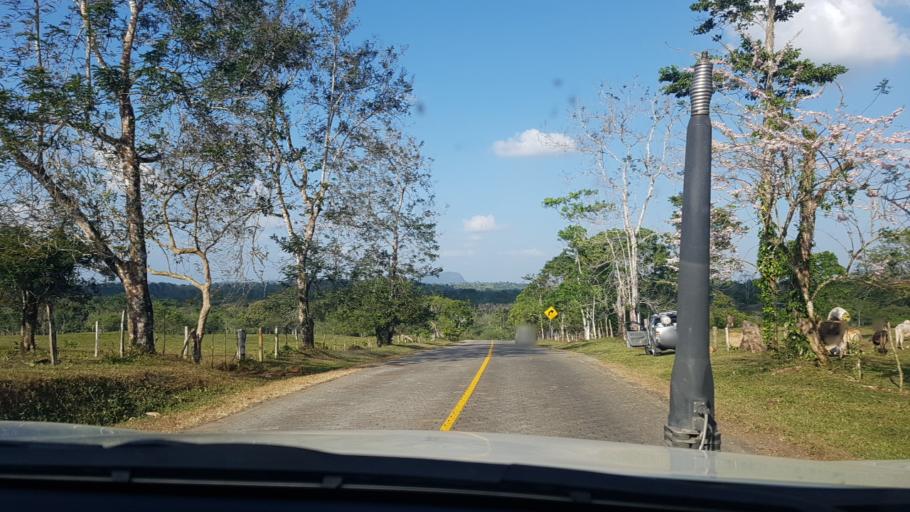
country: NI
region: Atlantico Sur
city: Nueva Guinea
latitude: 11.6935
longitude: -84.4143
